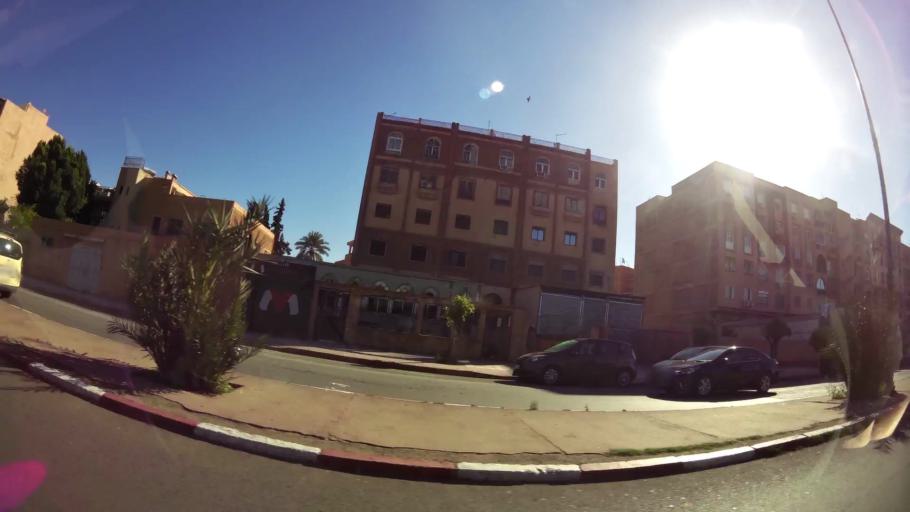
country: MA
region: Marrakech-Tensift-Al Haouz
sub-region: Marrakech
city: Marrakesh
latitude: 31.6502
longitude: -8.0148
